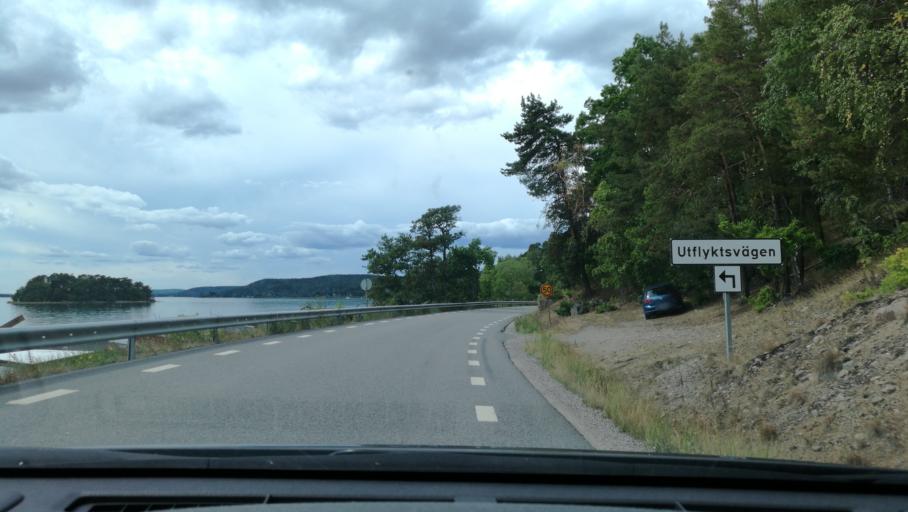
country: SE
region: OEstergoetland
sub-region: Norrkopings Kommun
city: Krokek
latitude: 58.6606
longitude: 16.3741
